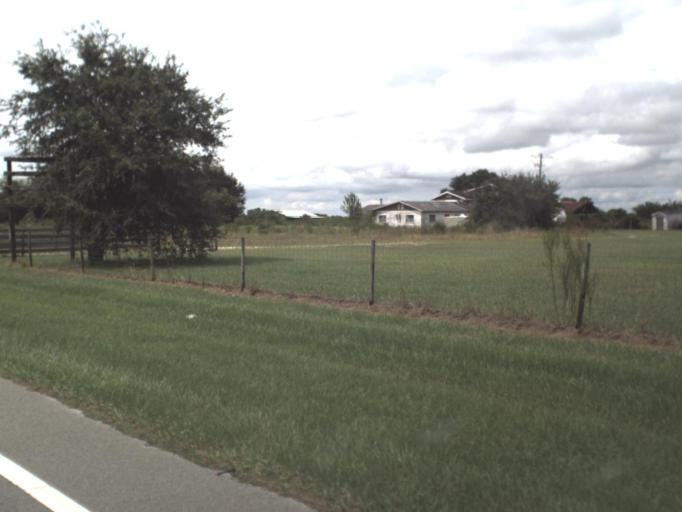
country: US
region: Florida
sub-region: Hillsborough County
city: Wimauma
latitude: 27.5856
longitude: -82.2168
